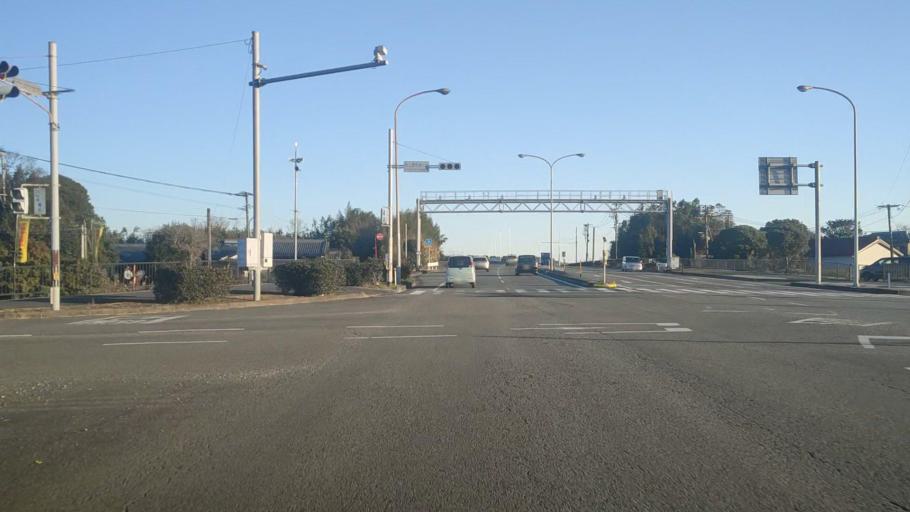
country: JP
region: Miyazaki
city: Tsuma
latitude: 32.0444
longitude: 131.4706
